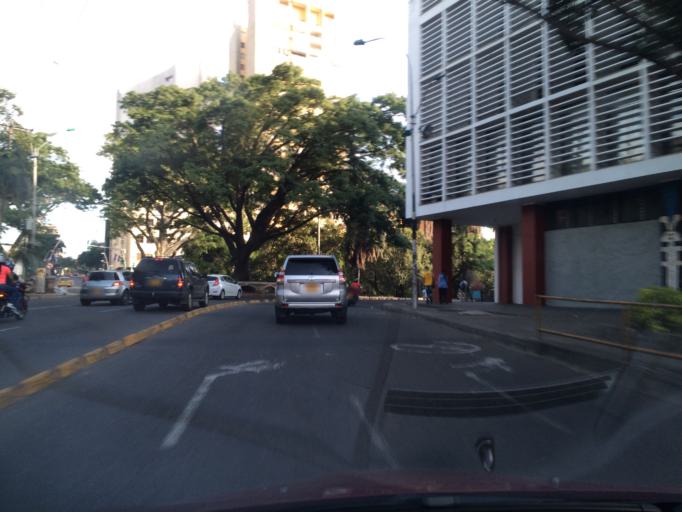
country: CO
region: Valle del Cauca
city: Cali
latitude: 3.4532
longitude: -76.5360
